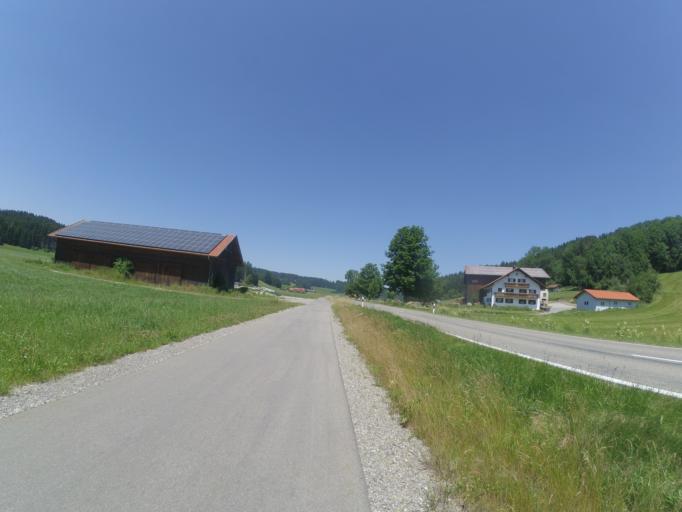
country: DE
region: Bavaria
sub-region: Swabia
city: Untrasried
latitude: 47.8363
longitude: 10.3588
